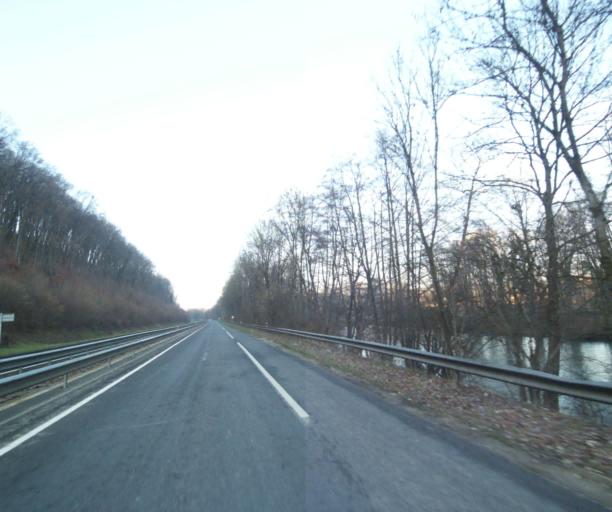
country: FR
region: Champagne-Ardenne
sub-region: Departement de la Haute-Marne
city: Chevillon
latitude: 48.5351
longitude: 5.0980
